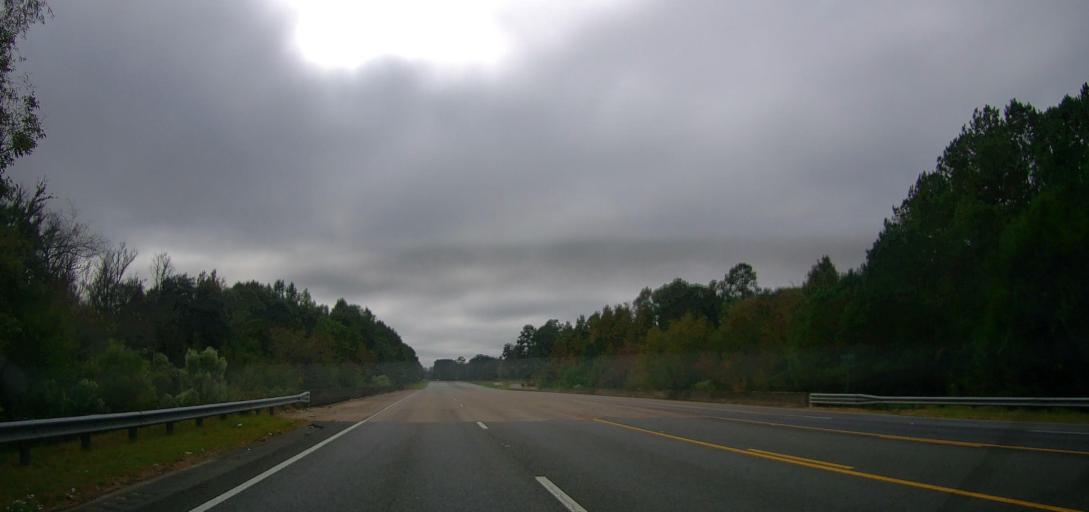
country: US
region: Georgia
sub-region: Thomas County
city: Thomasville
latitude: 30.9745
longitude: -83.8880
